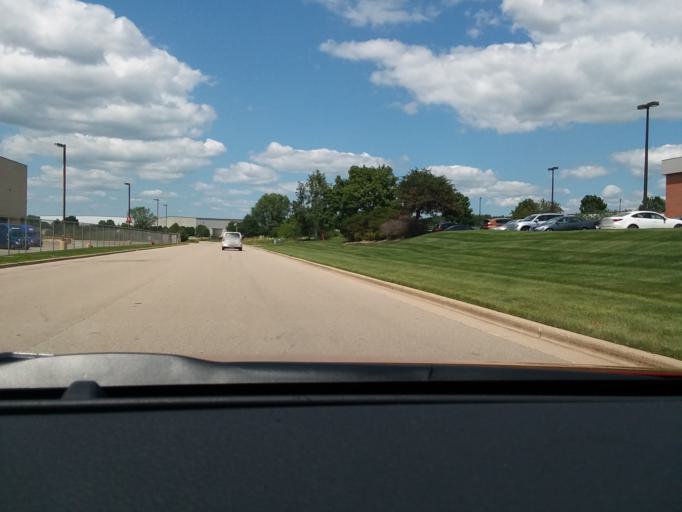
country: US
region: Wisconsin
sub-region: Dane County
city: Windsor
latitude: 43.1965
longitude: -89.3331
